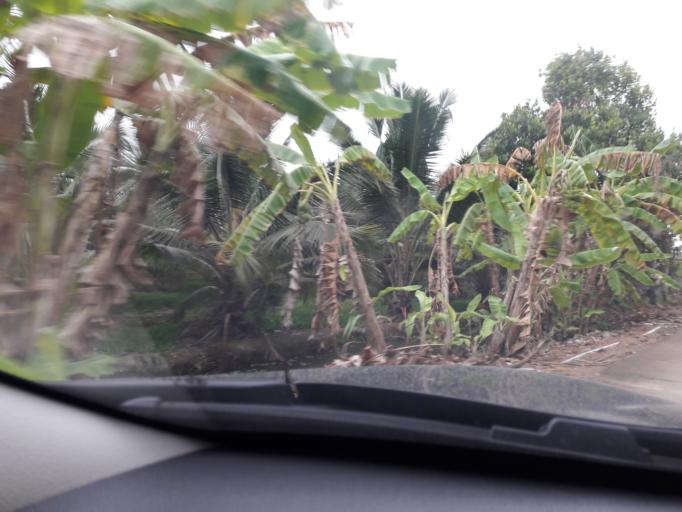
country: TH
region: Ratchaburi
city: Bang Phae
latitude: 13.6267
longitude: 99.9465
